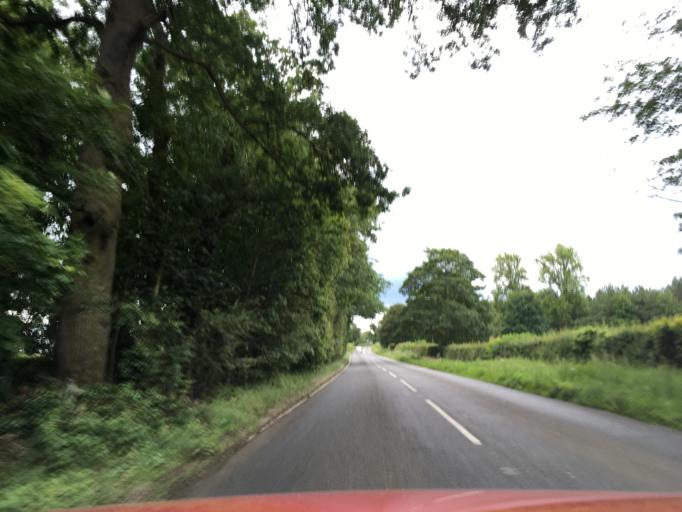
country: GB
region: England
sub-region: Central Bedfordshire
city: Potsgrove
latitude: 51.9716
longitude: -0.6423
